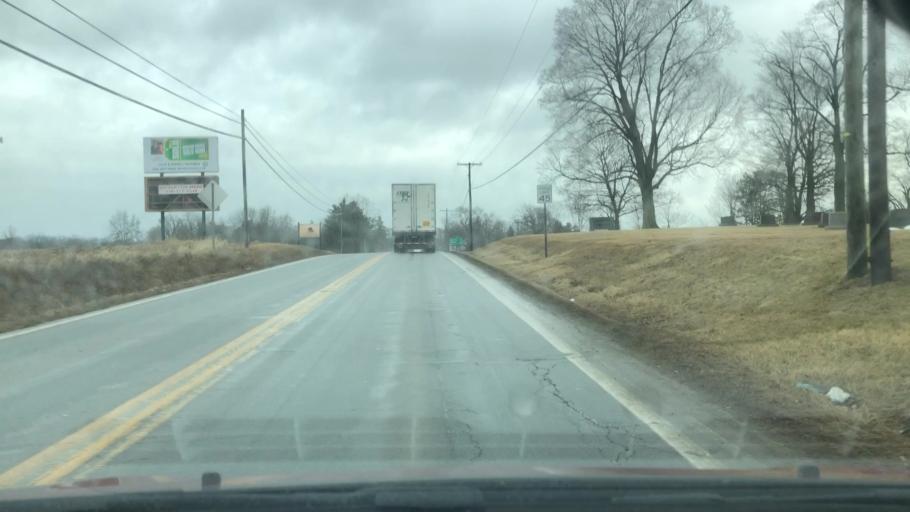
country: US
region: Ohio
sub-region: Wayne County
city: Smithville
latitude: 40.8702
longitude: -81.8483
